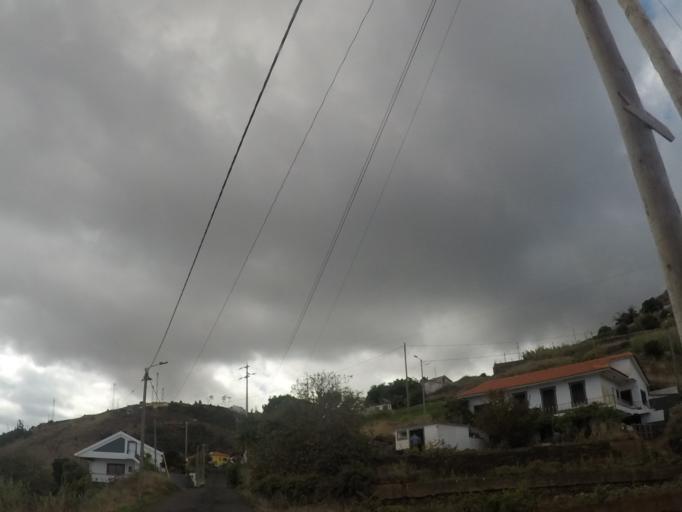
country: PT
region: Madeira
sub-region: Santa Cruz
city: Camacha
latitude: 32.6637
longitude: -16.8259
